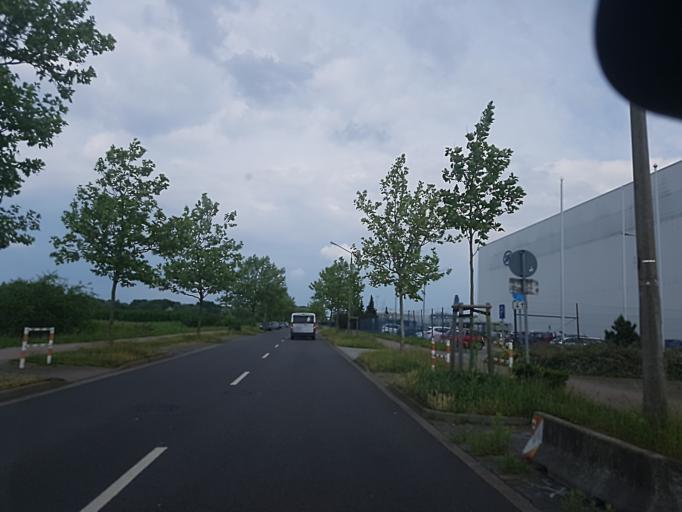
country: DE
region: Saxony-Anhalt
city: Nudersdorf
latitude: 51.8852
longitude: 12.5659
